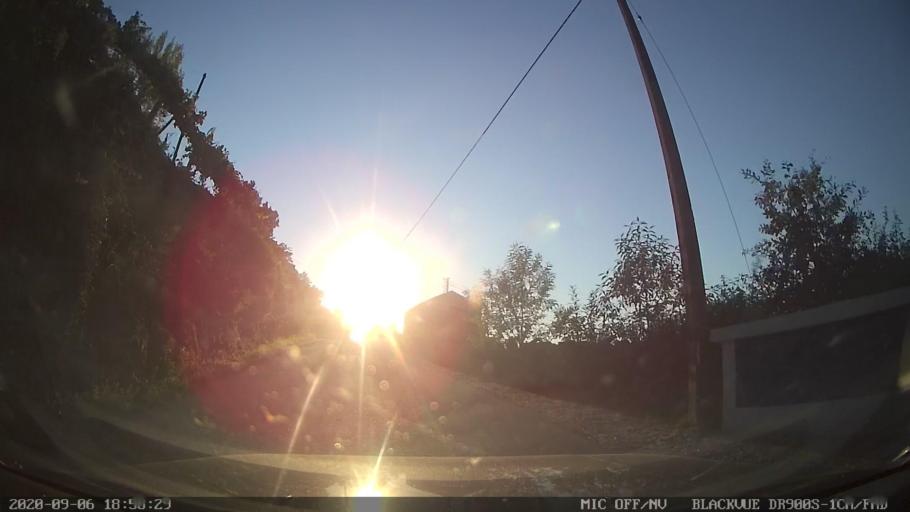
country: PT
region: Porto
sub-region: Baiao
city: Baiao
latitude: 41.2434
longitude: -7.9915
